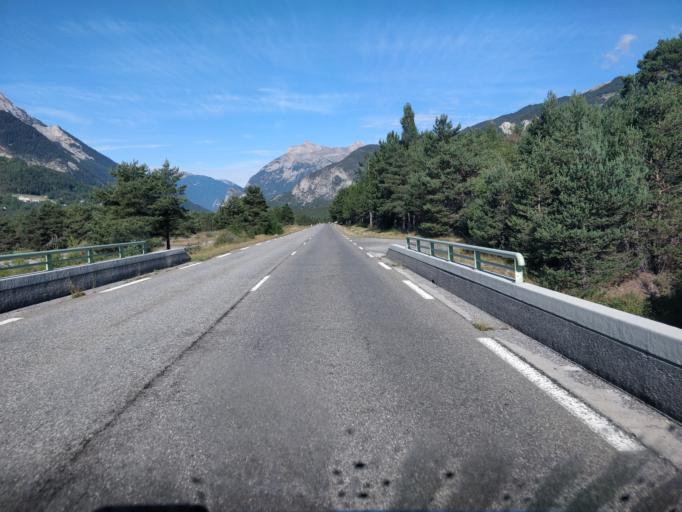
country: FR
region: Provence-Alpes-Cote d'Azur
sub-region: Departement des Alpes-de-Haute-Provence
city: Barcelonnette
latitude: 44.3869
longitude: 6.6012
